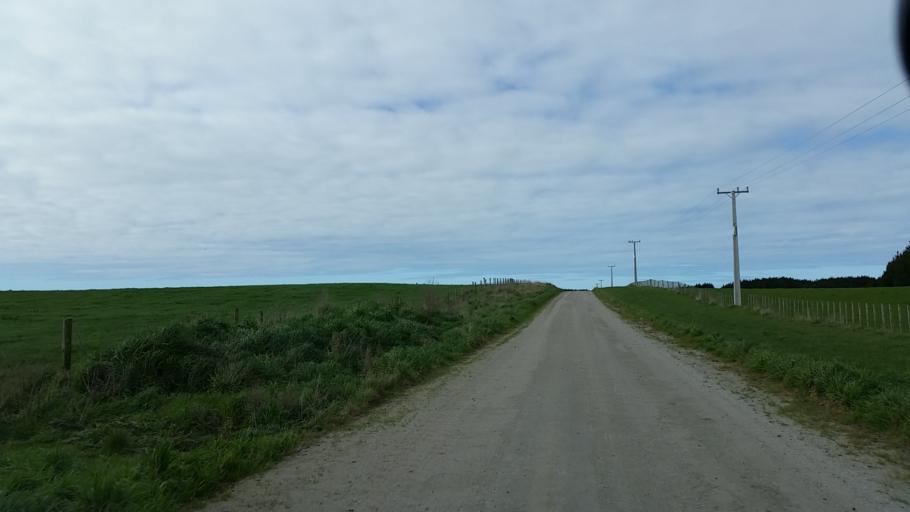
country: NZ
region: Taranaki
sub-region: South Taranaki District
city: Patea
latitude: -39.8061
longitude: 174.6963
